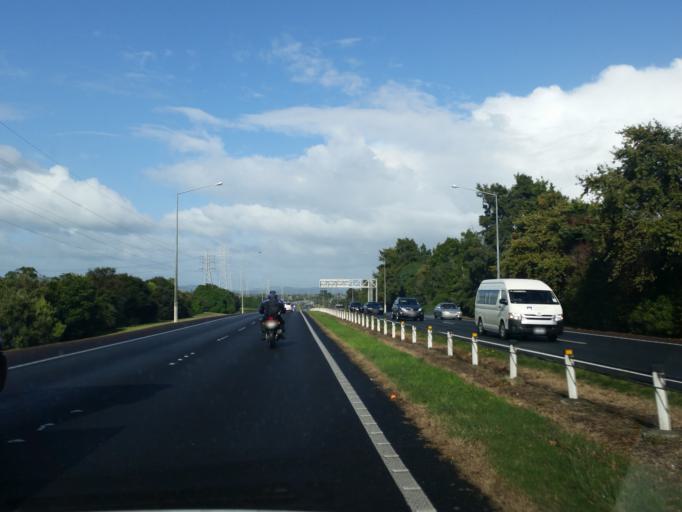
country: NZ
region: Auckland
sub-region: Auckland
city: Takanini
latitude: -37.0486
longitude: 174.9157
